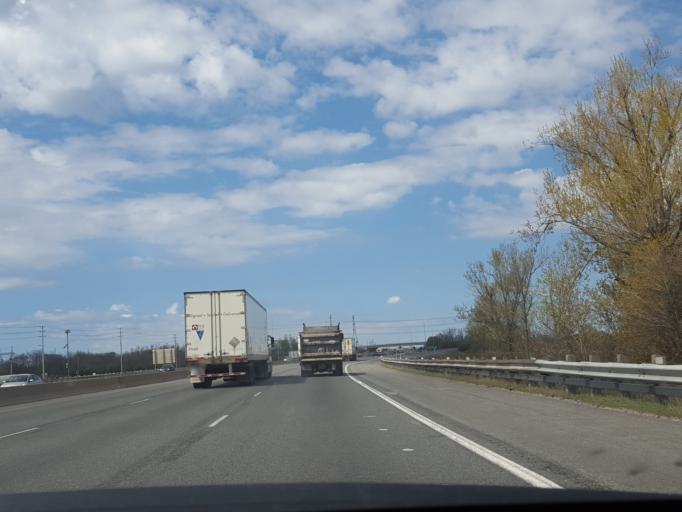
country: CA
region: Ontario
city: Oshawa
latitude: 43.8861
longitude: -78.7091
